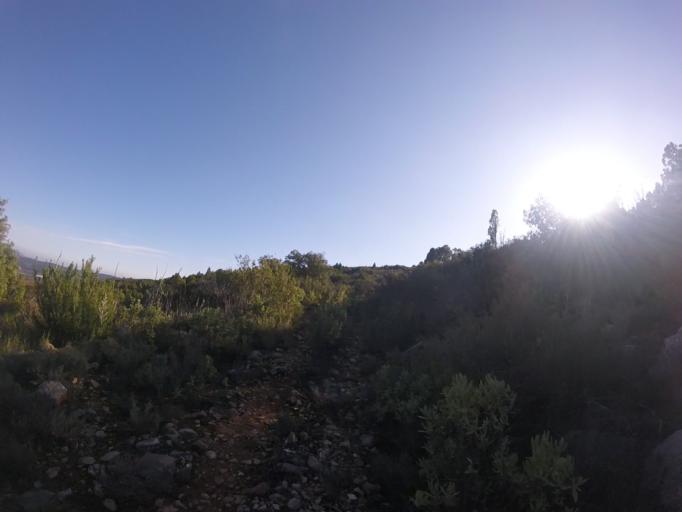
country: ES
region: Valencia
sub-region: Provincia de Castello
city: Sarratella
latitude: 40.2920
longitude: 0.0511
